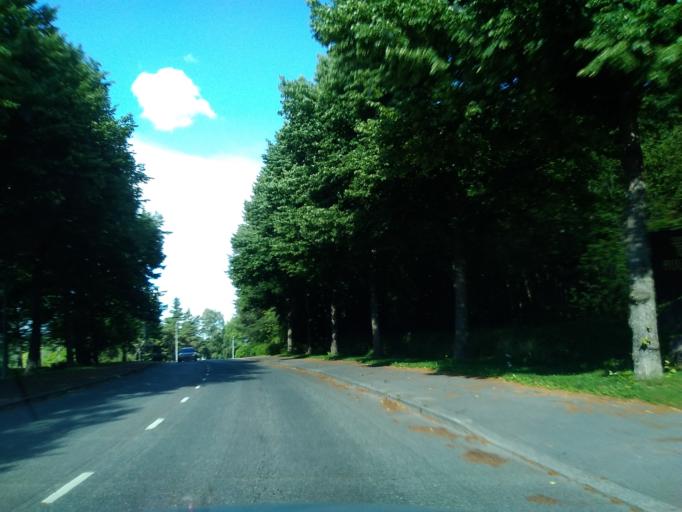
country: FI
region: Haeme
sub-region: Haemeenlinna
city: Haemeenlinna
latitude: 61.0138
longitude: 24.4593
